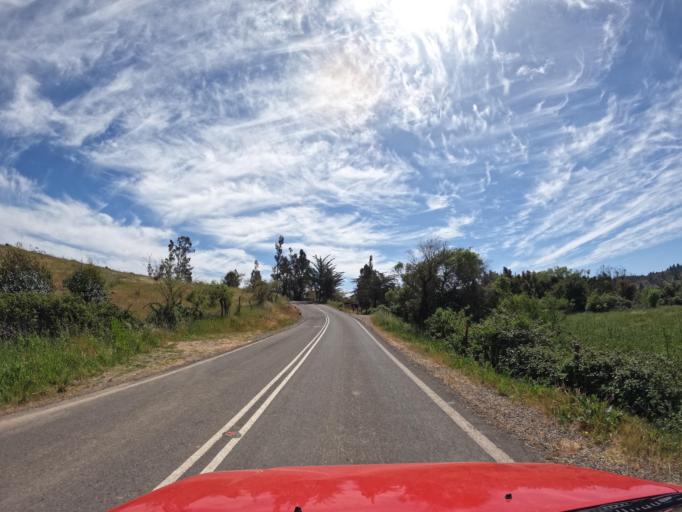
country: CL
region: Maule
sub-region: Provincia de Talca
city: Talca
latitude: -34.9910
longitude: -71.8562
